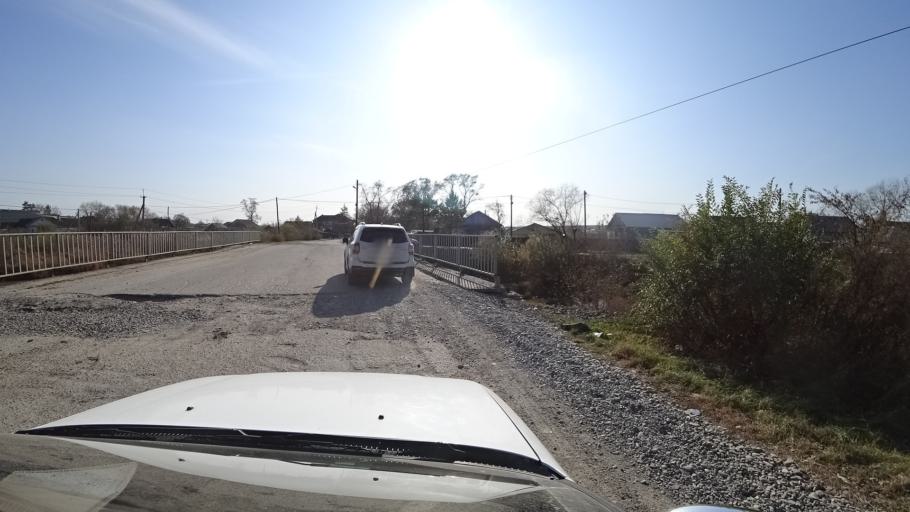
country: RU
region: Primorskiy
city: Dal'nerechensk
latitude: 45.9252
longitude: 133.7265
